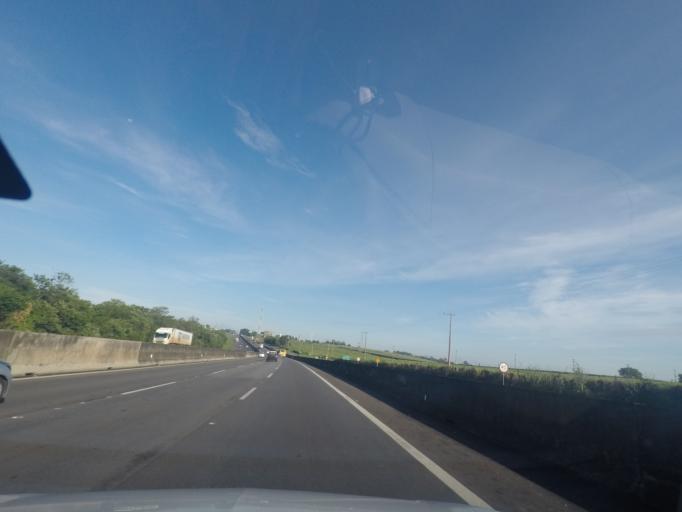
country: BR
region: Sao Paulo
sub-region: Nova Odessa
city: Nova Odessa
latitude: -22.7414
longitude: -47.2710
